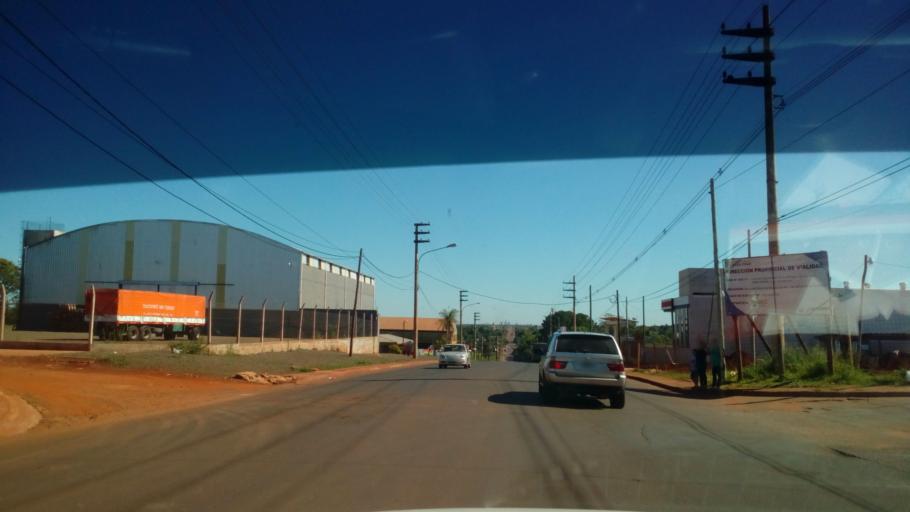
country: AR
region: Misiones
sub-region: Departamento de Capital
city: Posadas
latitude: -27.4148
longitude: -55.9125
